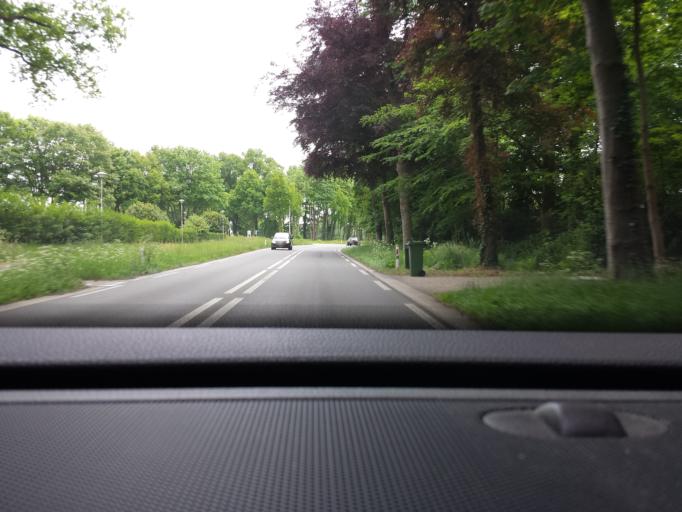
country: NL
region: Gelderland
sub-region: Gemeente Bronckhorst
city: Zelhem
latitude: 51.9946
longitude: 6.3453
